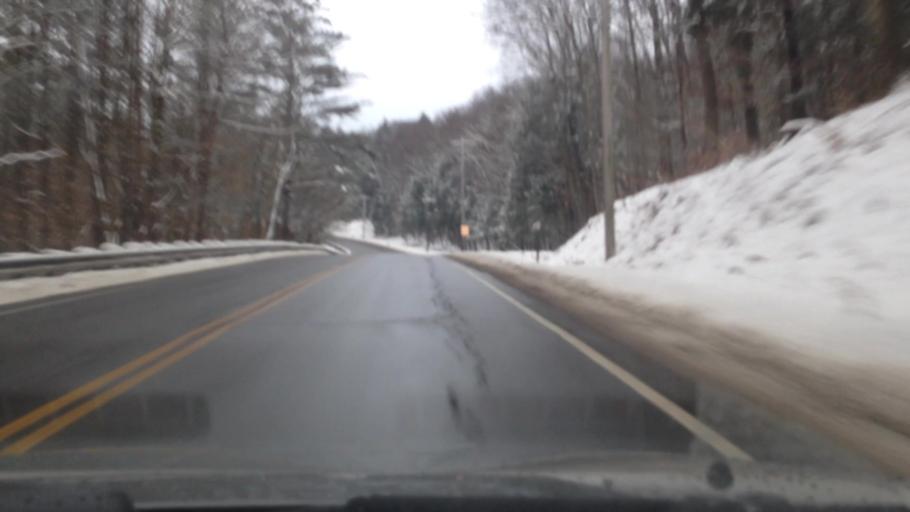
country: US
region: New Hampshire
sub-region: Cheshire County
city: Keene
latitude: 43.0364
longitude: -72.2701
